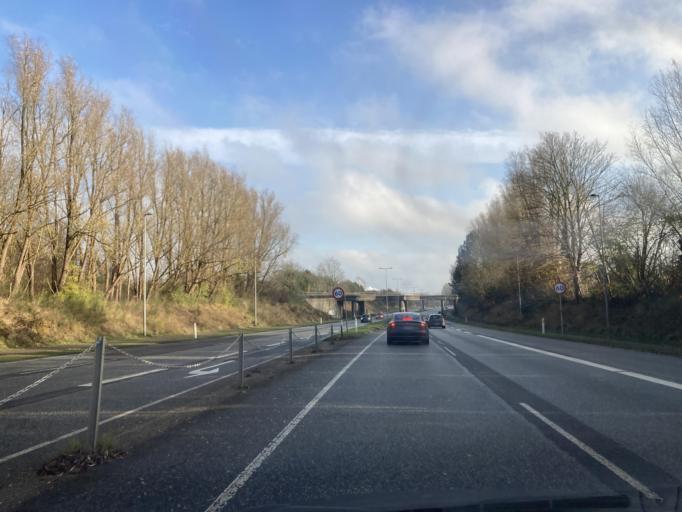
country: DK
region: Zealand
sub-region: Guldborgsund Kommune
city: Nykobing Falster
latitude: 54.7583
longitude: 11.8406
